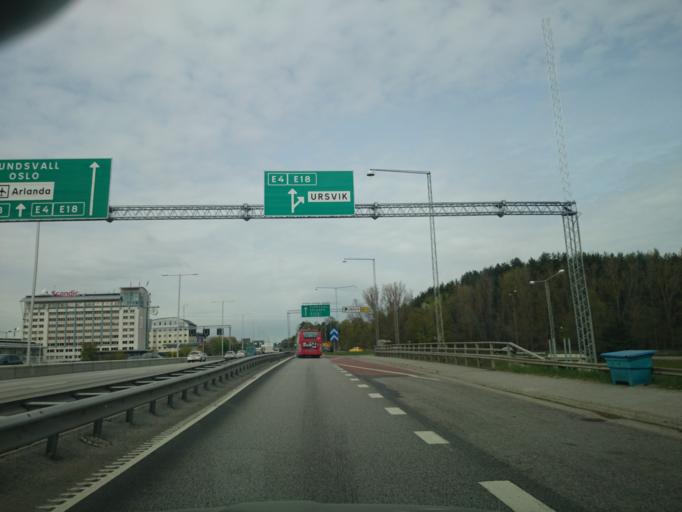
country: SE
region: Stockholm
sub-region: Norrtalje Kommun
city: Bergshamra
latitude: 59.3782
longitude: 18.0133
